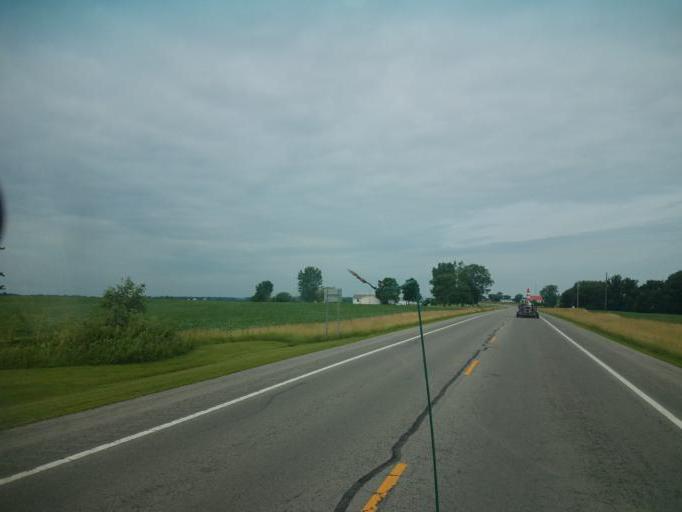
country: US
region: Ohio
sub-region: Hardin County
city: Kenton
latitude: 40.6870
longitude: -83.6872
